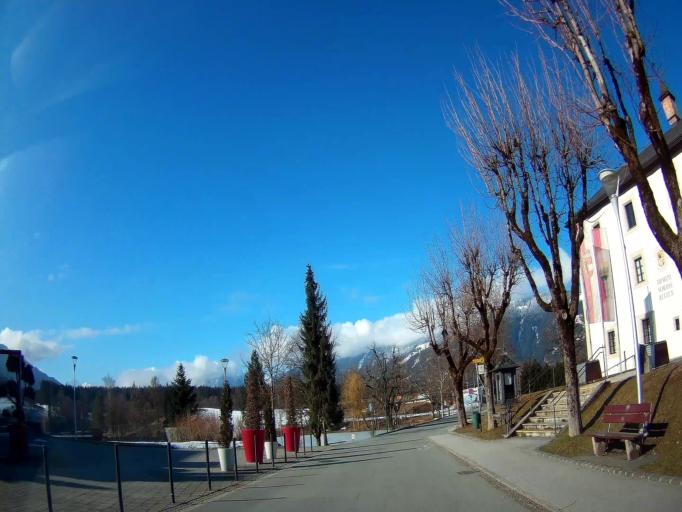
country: AT
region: Salzburg
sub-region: Politischer Bezirk Zell am See
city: Saalfelden am Steinernen Meer
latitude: 47.4210
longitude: 12.8468
